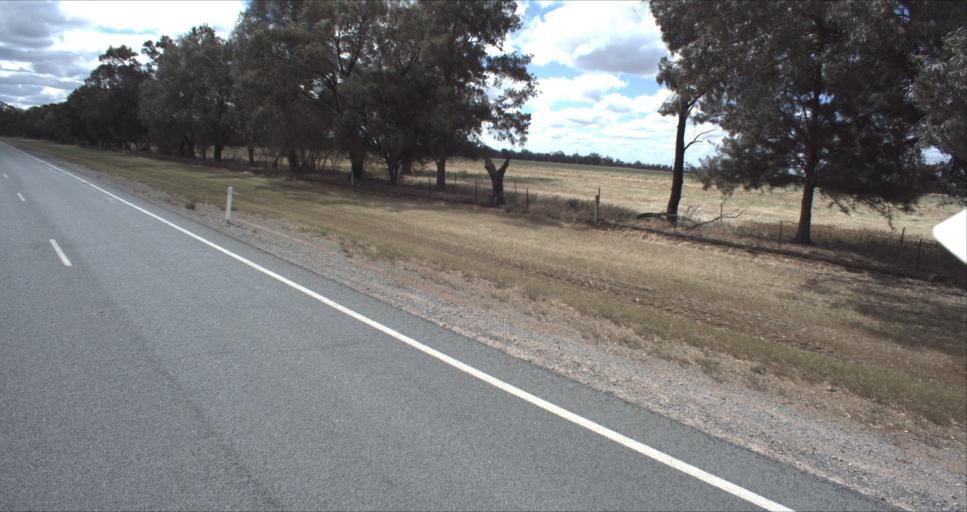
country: AU
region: New South Wales
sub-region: Leeton
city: Leeton
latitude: -34.6244
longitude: 146.3879
